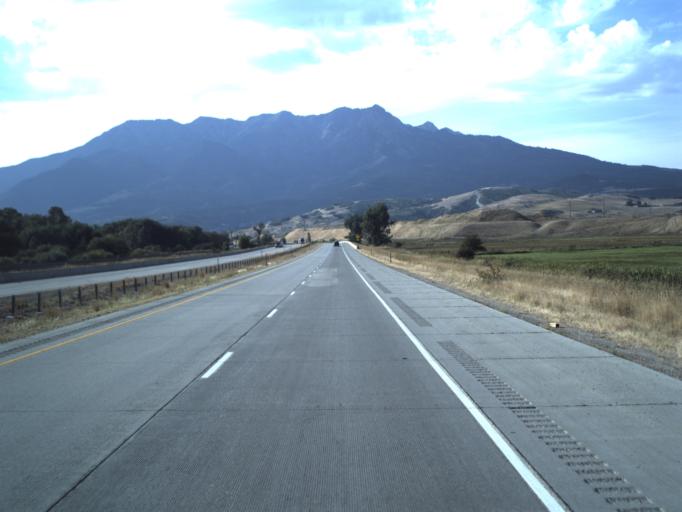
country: US
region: Utah
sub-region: Morgan County
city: Mountain Green
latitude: 41.1328
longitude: -111.7801
